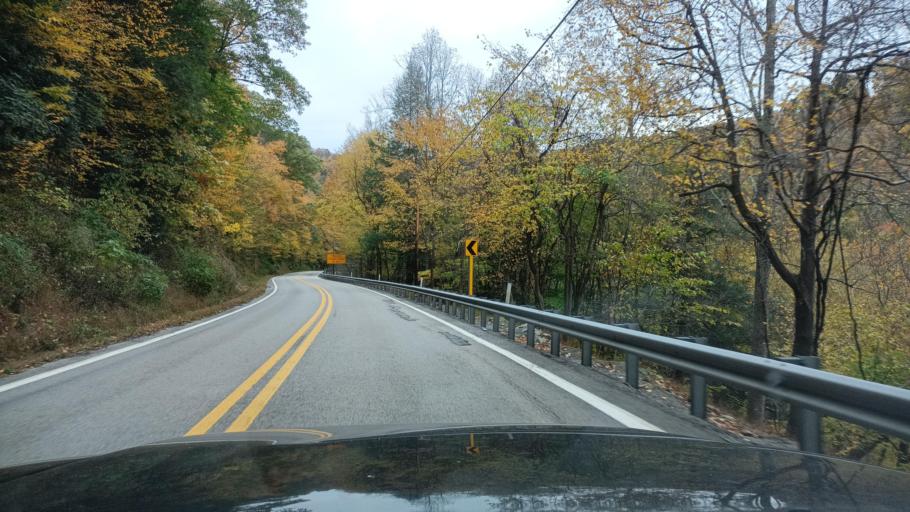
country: US
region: West Virginia
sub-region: Preston County
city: Terra Alta
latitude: 39.2942
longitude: -79.6280
